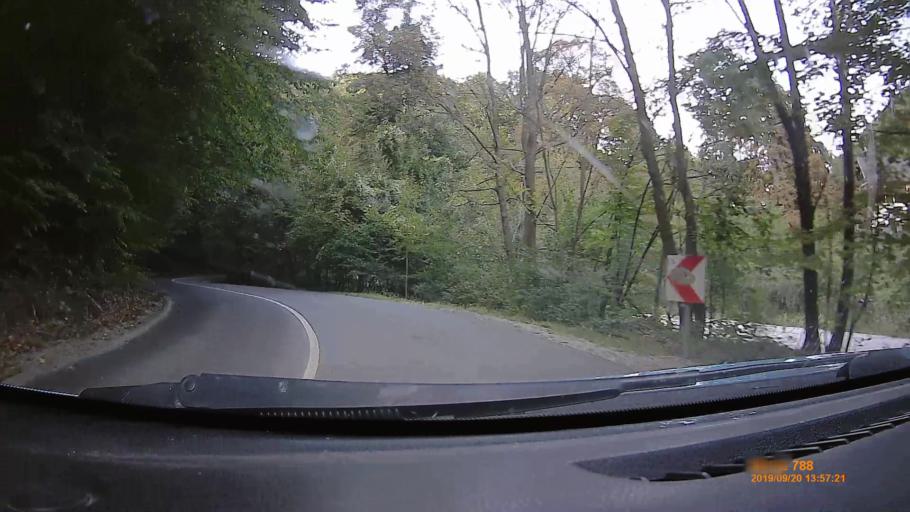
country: HU
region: Borsod-Abauj-Zemplen
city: Sajobabony
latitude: 48.0916
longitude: 20.6195
